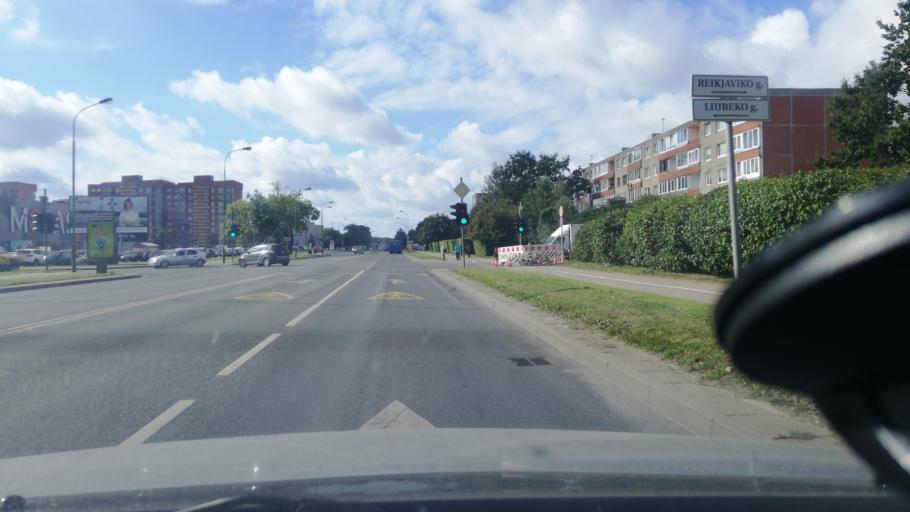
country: LT
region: Klaipedos apskritis
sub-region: Klaipeda
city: Klaipeda
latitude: 55.6671
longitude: 21.1779
